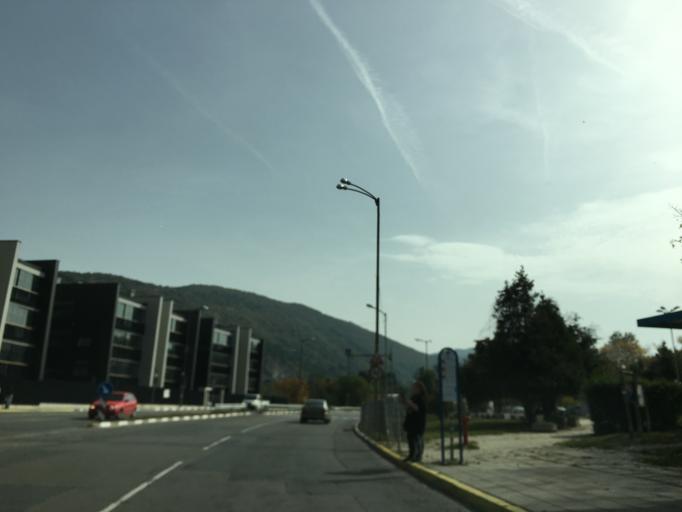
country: BG
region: Sofia-Capital
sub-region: Stolichna Obshtina
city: Sofia
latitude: 42.5964
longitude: 23.4131
